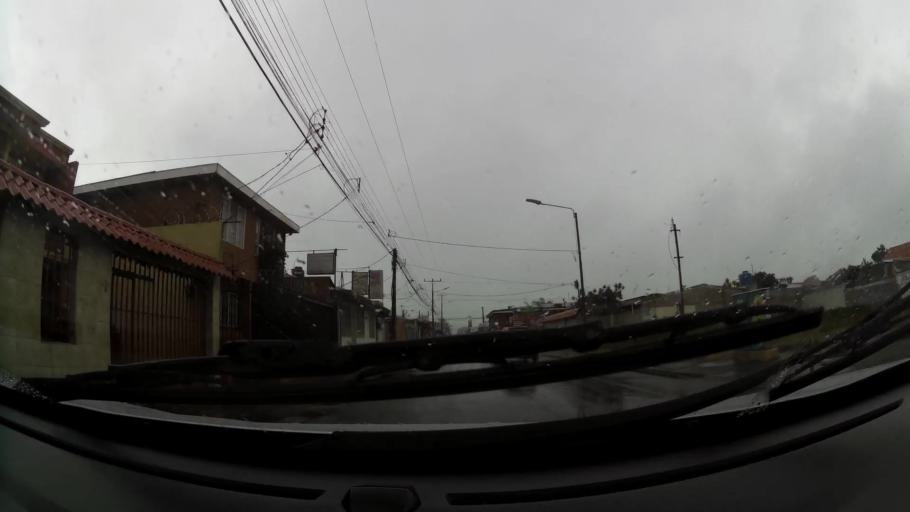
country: CR
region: Cartago
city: Cartago
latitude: 9.8661
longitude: -83.9298
